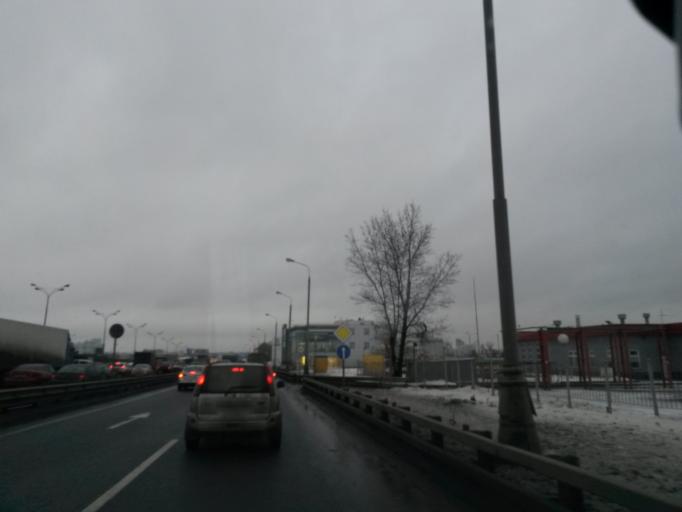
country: RU
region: Moskovskaya
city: Zarech'ye
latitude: 55.6934
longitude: 37.4109
